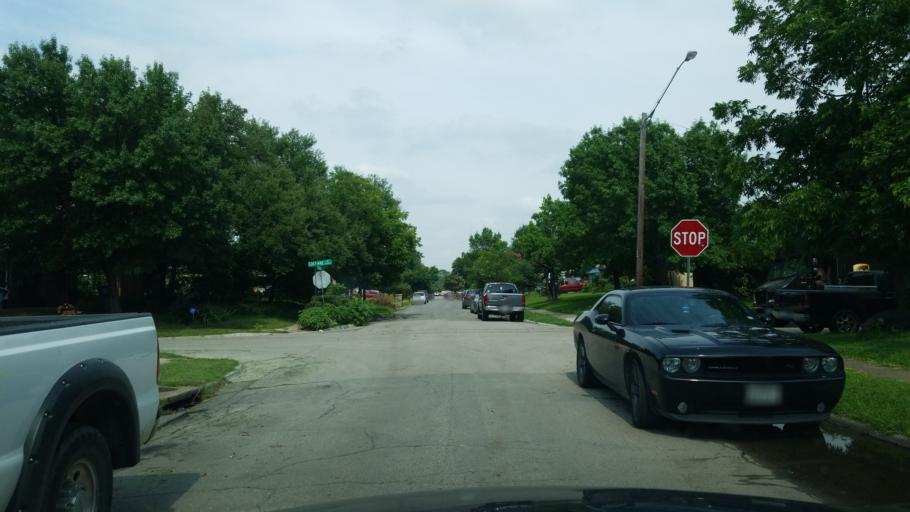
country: US
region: Texas
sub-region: Dallas County
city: Farmers Branch
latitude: 32.8987
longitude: -96.8782
